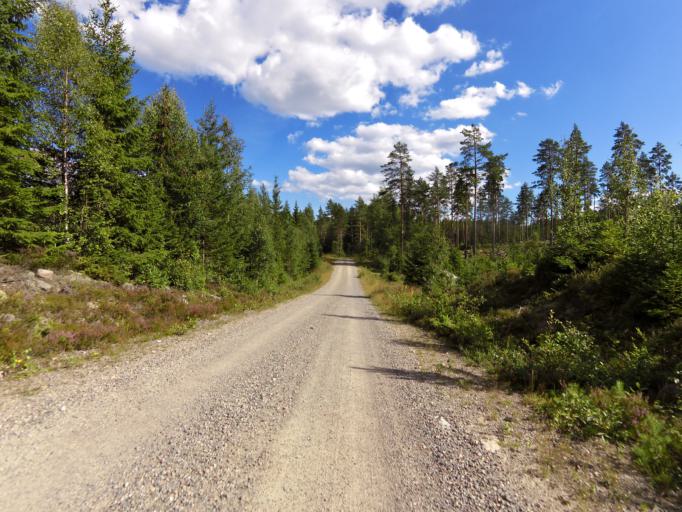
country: SE
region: Dalarna
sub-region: Faluns Kommun
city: Svardsjo
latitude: 60.6615
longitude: 15.9079
